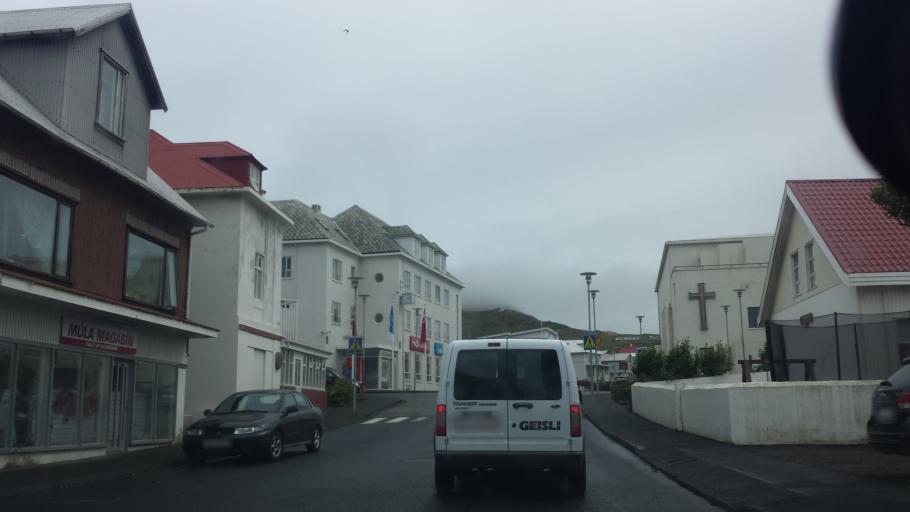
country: IS
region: South
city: Vestmannaeyjar
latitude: 63.4410
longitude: -20.2666
